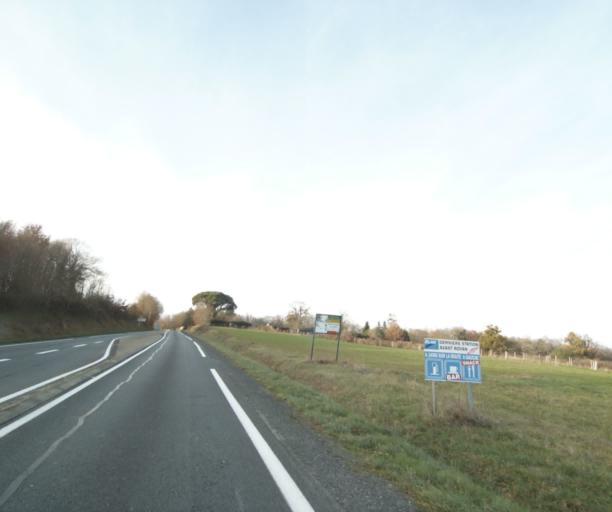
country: FR
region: Poitou-Charentes
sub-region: Departement de la Charente-Maritime
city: Chaniers
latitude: 45.7401
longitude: -0.5439
